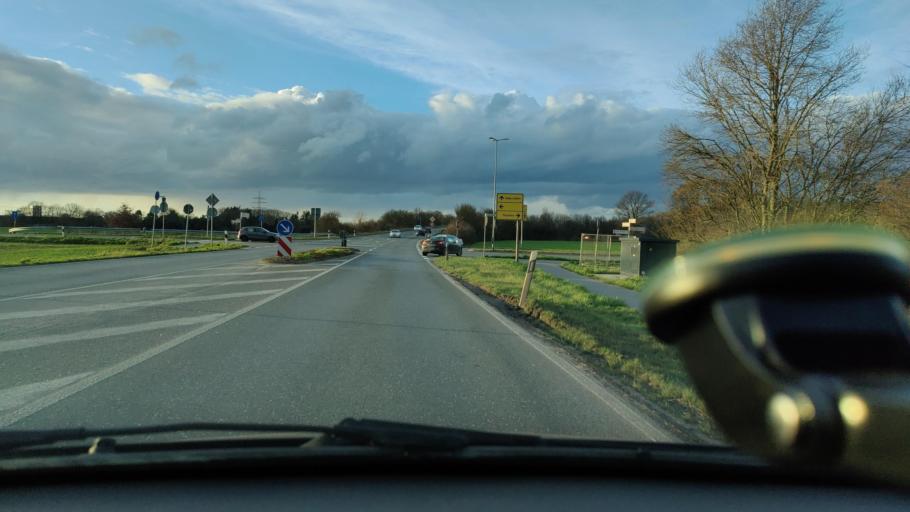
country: DE
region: North Rhine-Westphalia
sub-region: Regierungsbezirk Dusseldorf
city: Kamp-Lintfort
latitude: 51.4884
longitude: 6.5860
